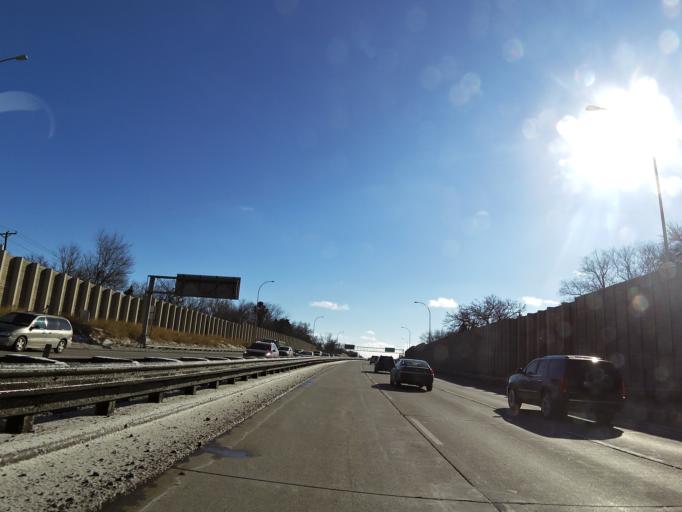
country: US
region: Minnesota
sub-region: Hennepin County
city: Saint Louis Park
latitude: 44.9218
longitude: -93.3494
